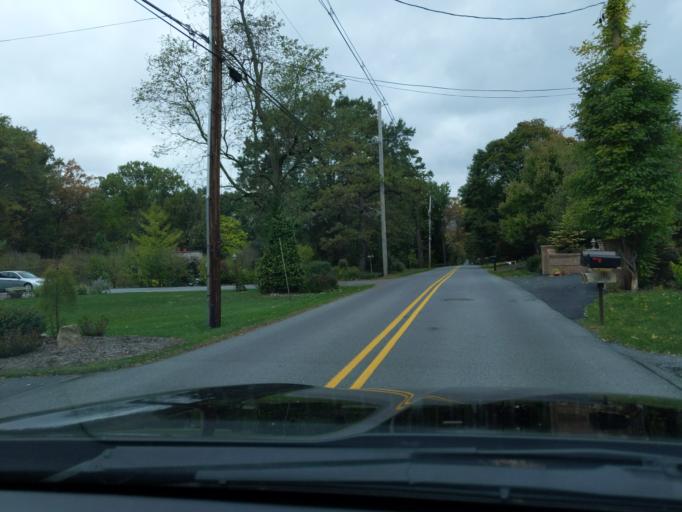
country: US
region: Pennsylvania
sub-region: Blair County
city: Hollidaysburg
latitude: 40.4497
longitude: -78.3874
